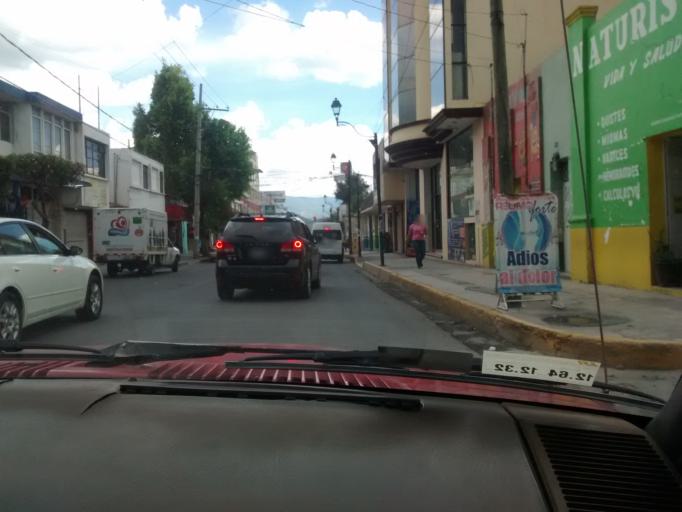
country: MX
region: Puebla
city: Tehuacan
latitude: 18.4627
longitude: -97.3860
